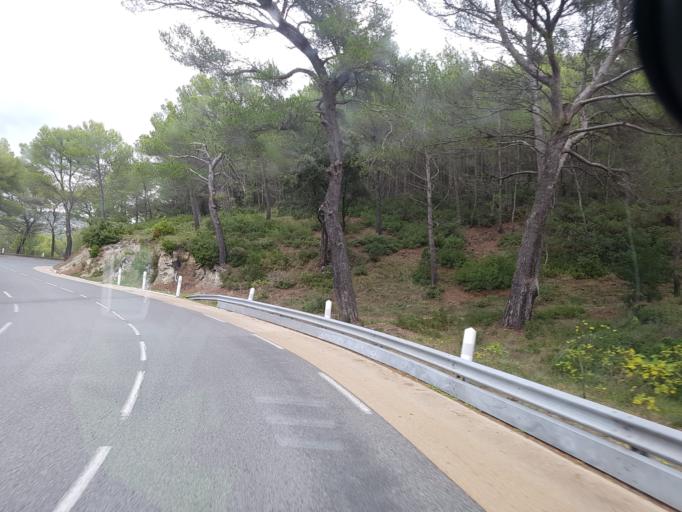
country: FR
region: Provence-Alpes-Cote d'Azur
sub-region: Departement des Bouches-du-Rhone
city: Cuges-les-Pins
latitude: 43.2663
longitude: 5.7331
